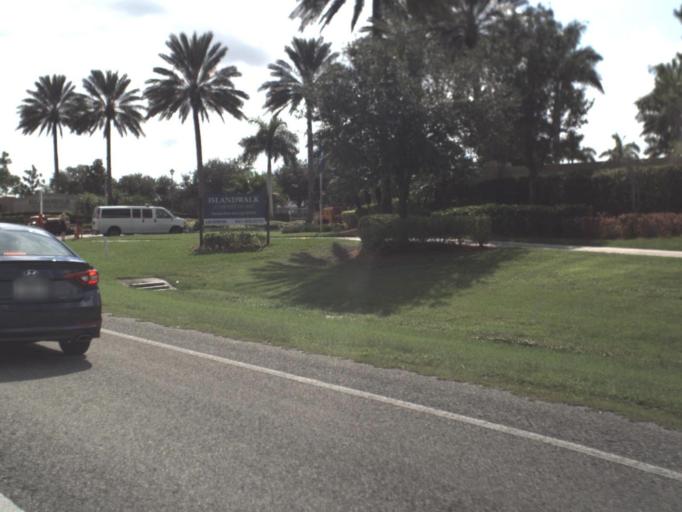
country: US
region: Florida
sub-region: Sarasota County
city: Plantation
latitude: 27.0495
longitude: -82.3439
